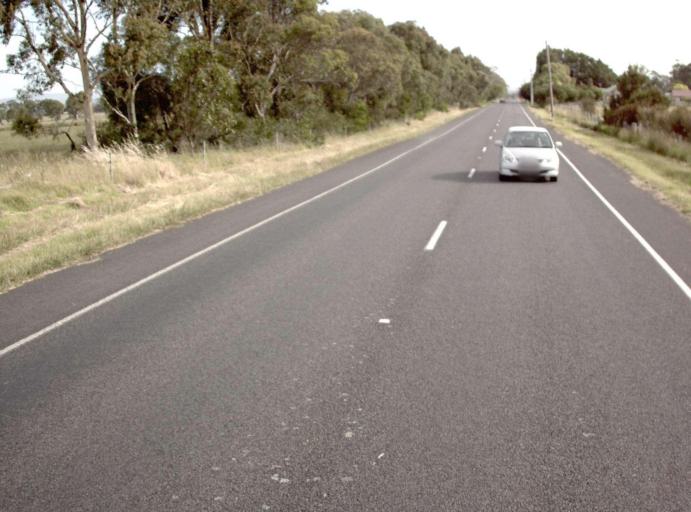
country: AU
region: Victoria
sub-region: Latrobe
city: Traralgon
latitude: -38.1356
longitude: 146.5577
